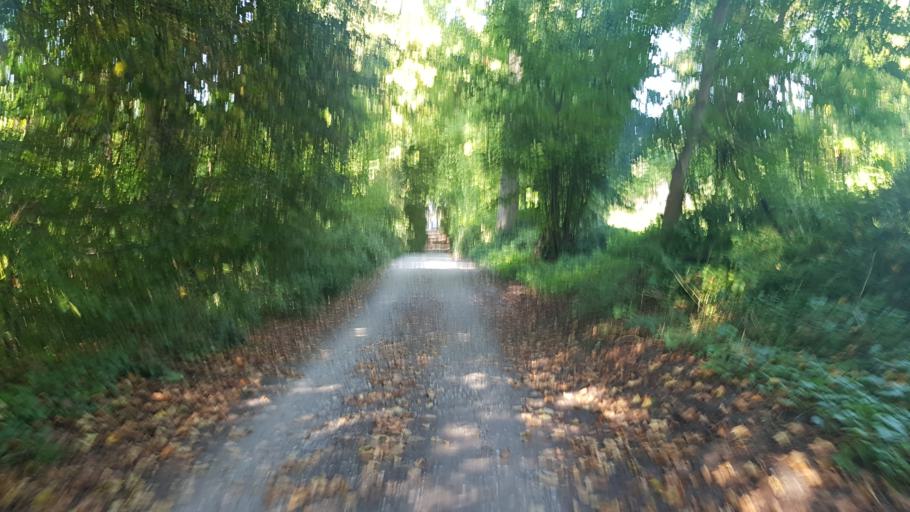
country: DE
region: Bavaria
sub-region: Upper Bavaria
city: Inning am Ammersee
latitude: 48.0478
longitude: 11.1356
